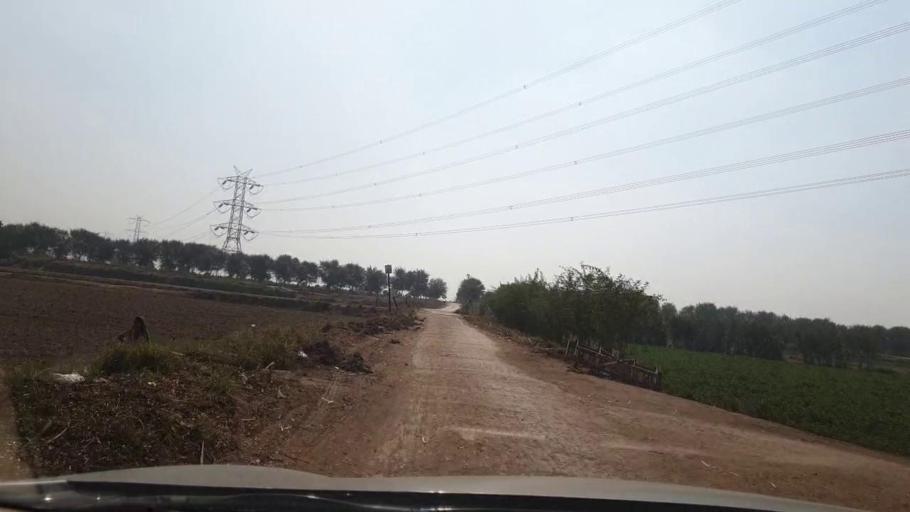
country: PK
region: Sindh
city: Tando Allahyar
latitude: 25.4749
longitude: 68.7451
